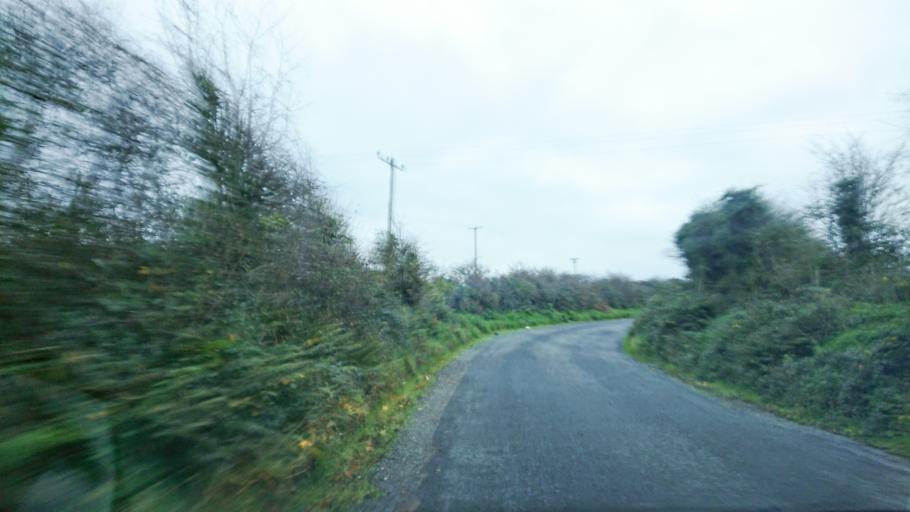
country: IE
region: Munster
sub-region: Waterford
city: Dunmore East
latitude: 52.2373
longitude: -6.9760
